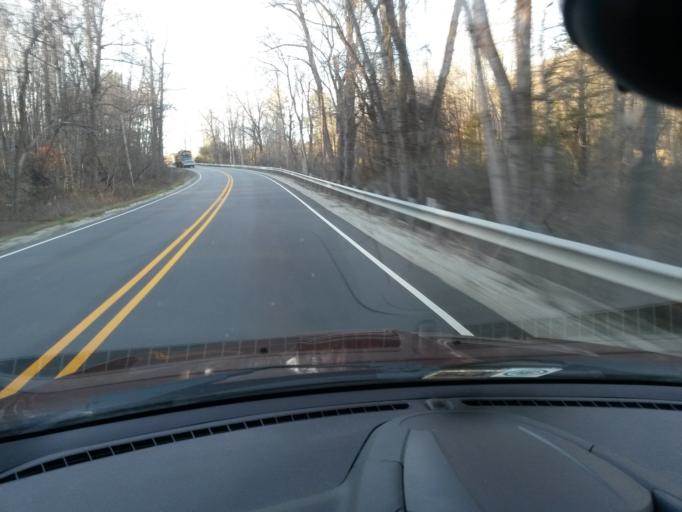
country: US
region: Virginia
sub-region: Amherst County
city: Amherst
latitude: 37.6219
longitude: -79.1066
